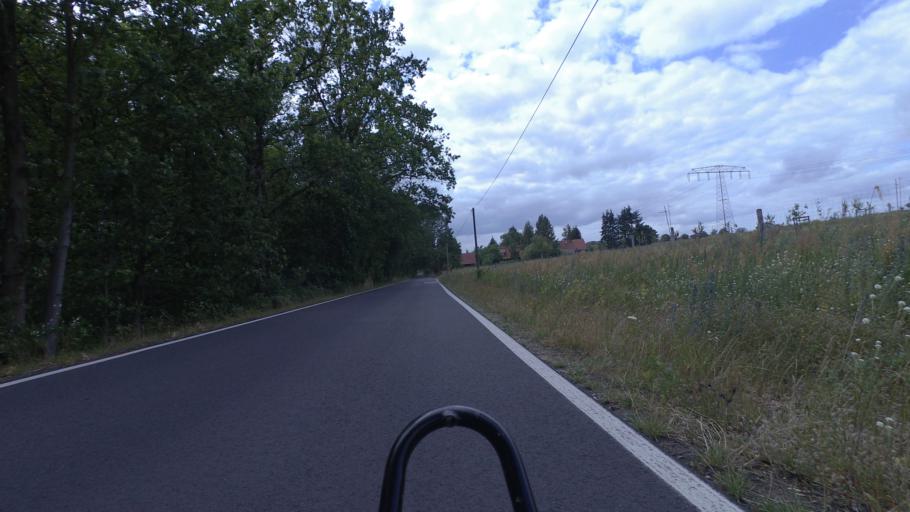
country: DE
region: Brandenburg
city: Ludwigsfelde
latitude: 52.2484
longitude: 13.2938
